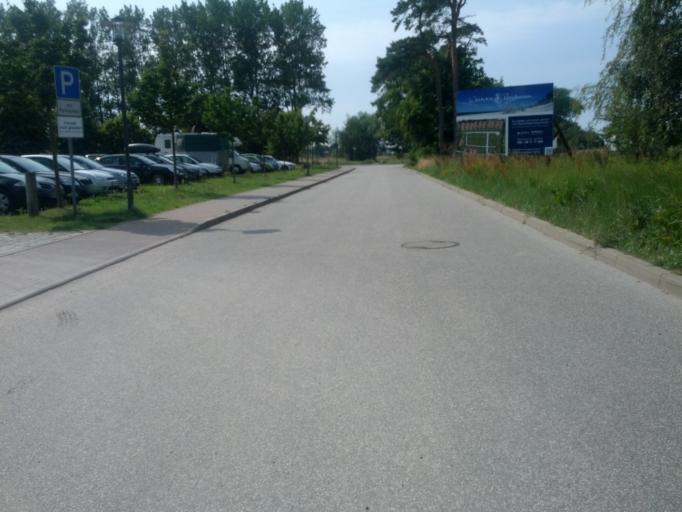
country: DE
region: Mecklenburg-Vorpommern
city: Bastorf
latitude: 54.1513
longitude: 11.7077
